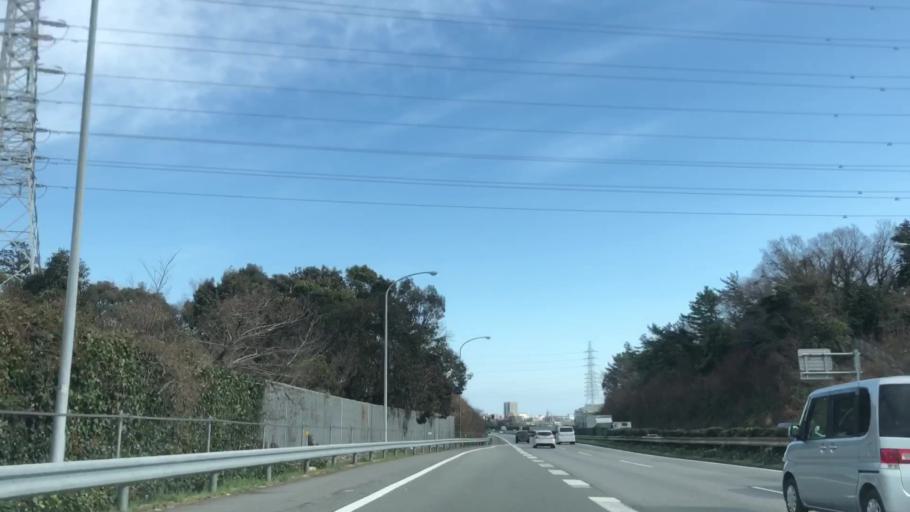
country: JP
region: Shizuoka
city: Hamamatsu
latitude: 34.7562
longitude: 137.7398
